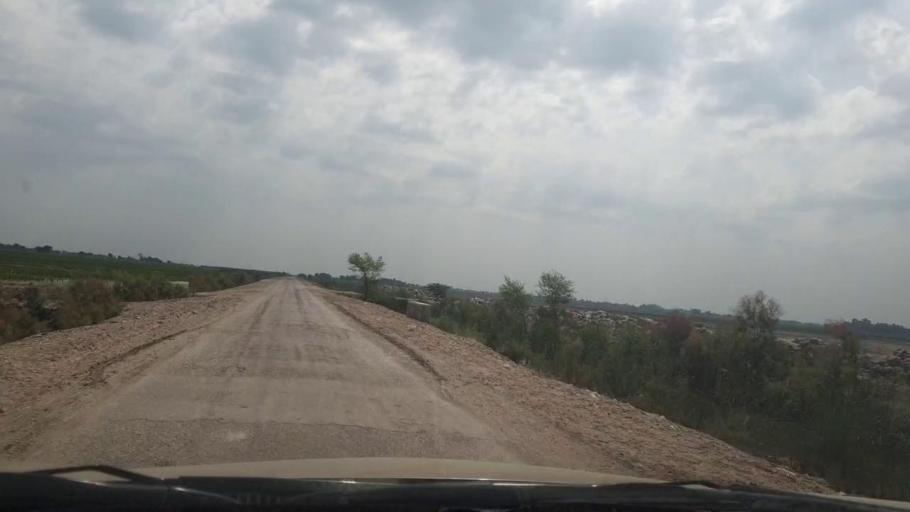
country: PK
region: Sindh
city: Ratodero
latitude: 27.6977
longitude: 68.2203
